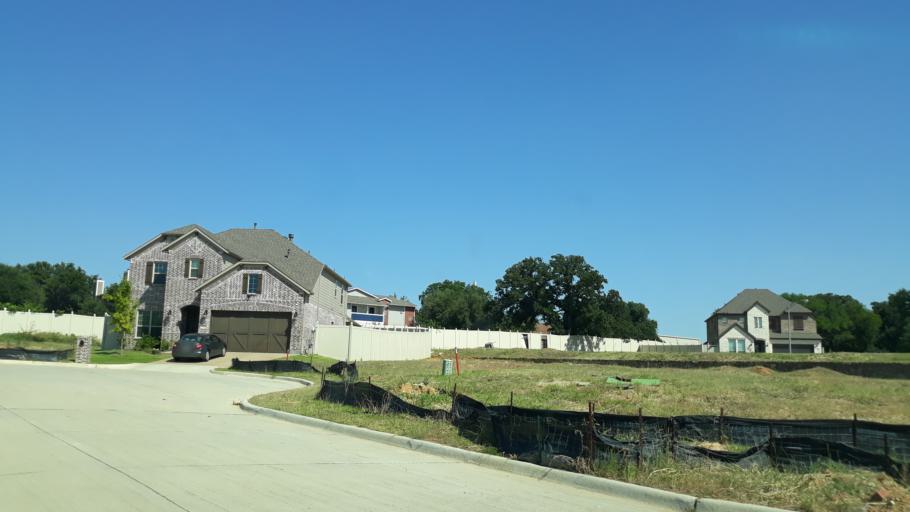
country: US
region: Texas
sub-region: Dallas County
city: Irving
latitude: 32.8312
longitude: -97.0125
